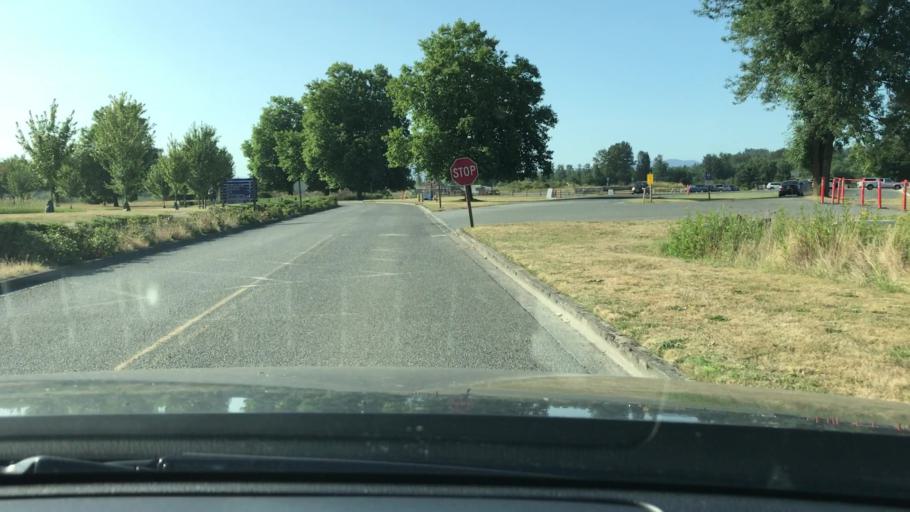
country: US
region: Washington
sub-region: King County
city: Redmond
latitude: 47.6621
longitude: -122.1111
